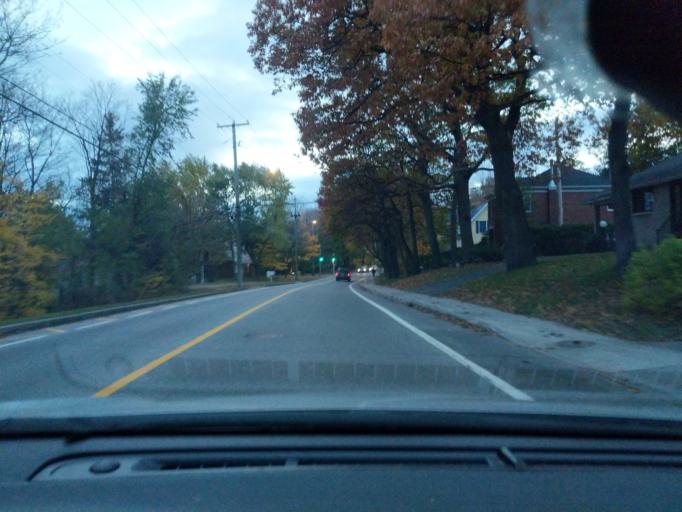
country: CA
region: Quebec
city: Quebec
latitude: 46.7705
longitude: -71.2619
